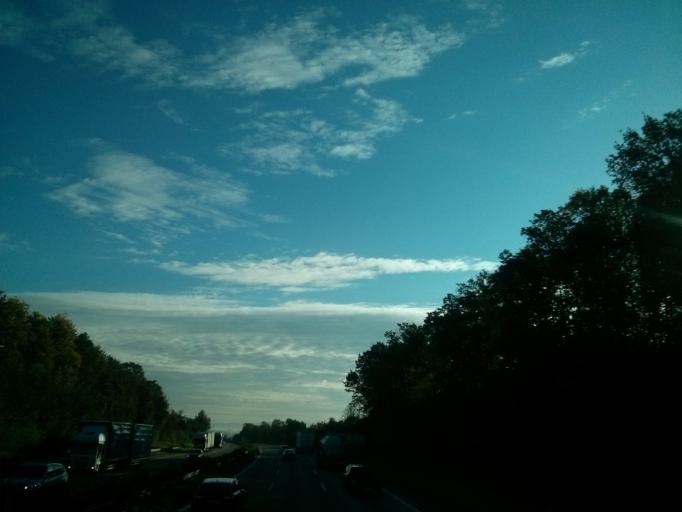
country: DE
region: Baden-Wuerttemberg
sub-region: Regierungsbezirk Stuttgart
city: Leingarten
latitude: 49.1861
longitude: 9.1338
